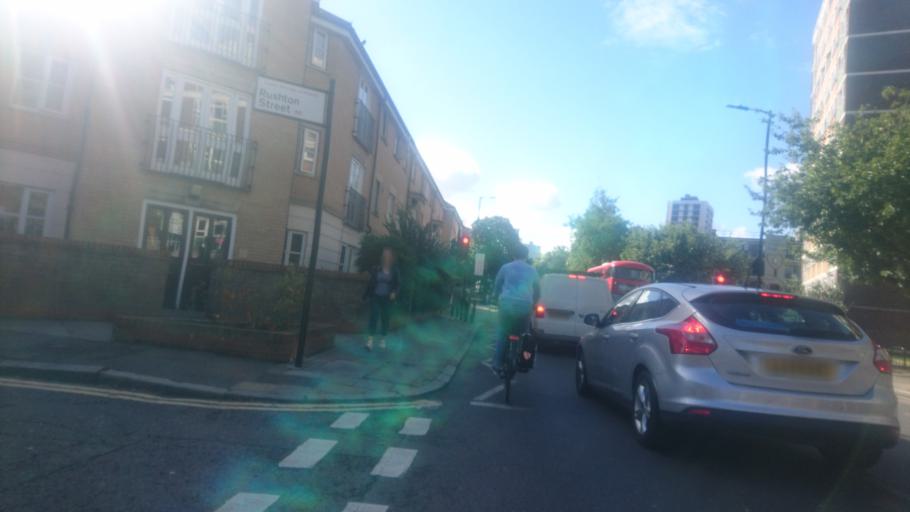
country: GB
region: England
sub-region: Greater London
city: Barbican
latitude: 51.5333
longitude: -0.0876
